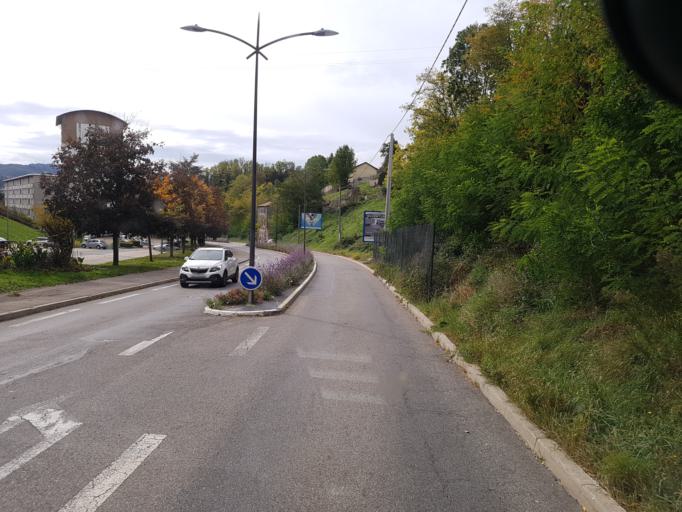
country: FR
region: Rhone-Alpes
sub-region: Departement de la Loire
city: Unieux
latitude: 45.4020
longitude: 4.2913
